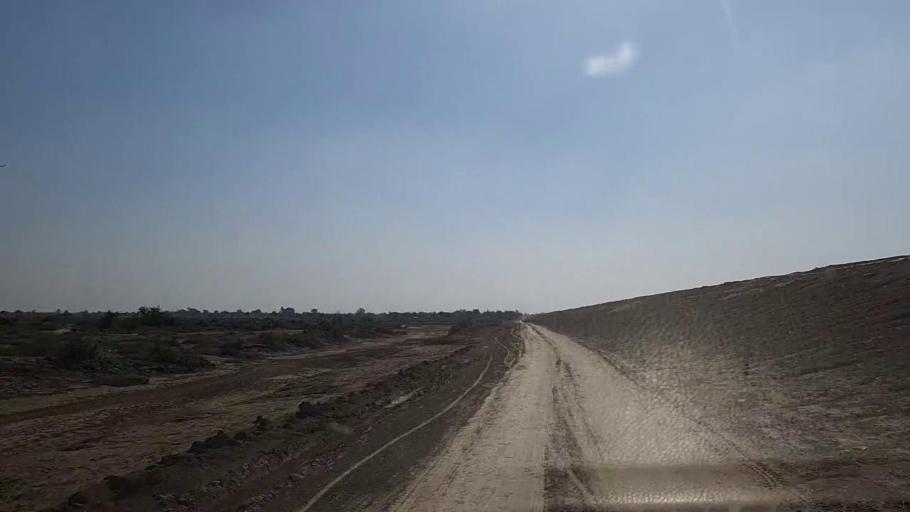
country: PK
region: Sindh
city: Daro Mehar
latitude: 24.7913
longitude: 68.0765
